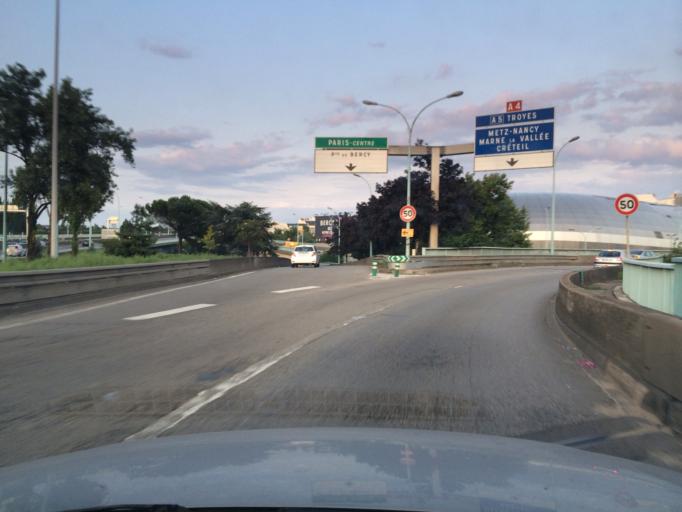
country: FR
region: Ile-de-France
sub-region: Departement du Val-de-Marne
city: Ivry-sur-Seine
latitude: 48.8267
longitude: 2.3902
